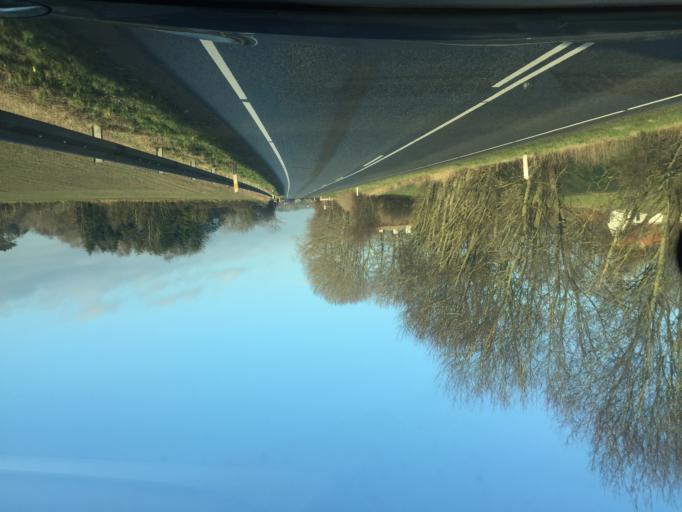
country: DK
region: South Denmark
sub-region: Faaborg-Midtfyn Kommune
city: Faaborg
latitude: 55.1688
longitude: 10.2807
